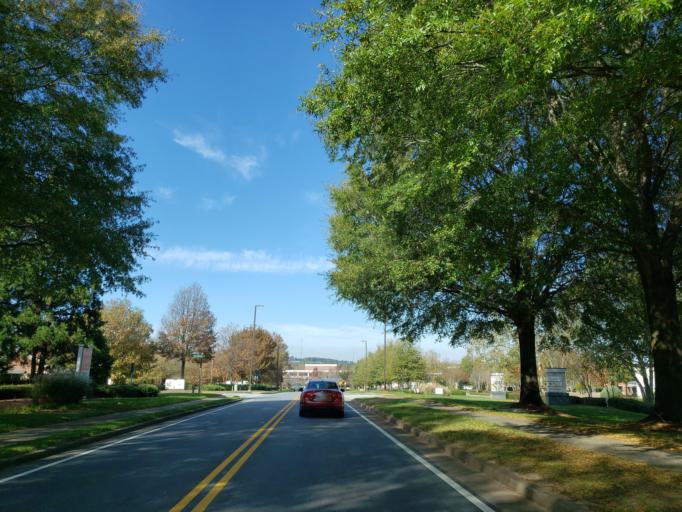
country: US
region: Georgia
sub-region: Fulton County
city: Alpharetta
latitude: 34.0358
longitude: -84.2908
